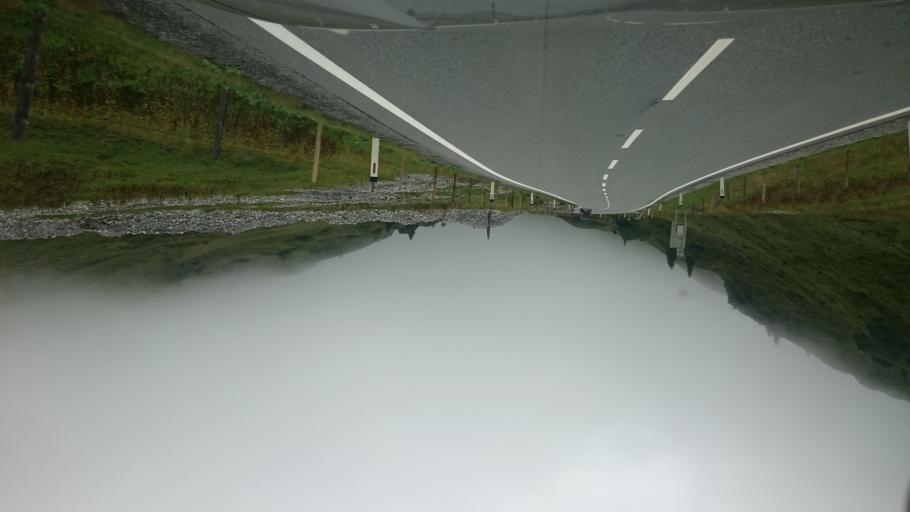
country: AT
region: Vorarlberg
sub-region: Politischer Bezirk Bludenz
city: Lech
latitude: 47.1562
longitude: 10.1647
